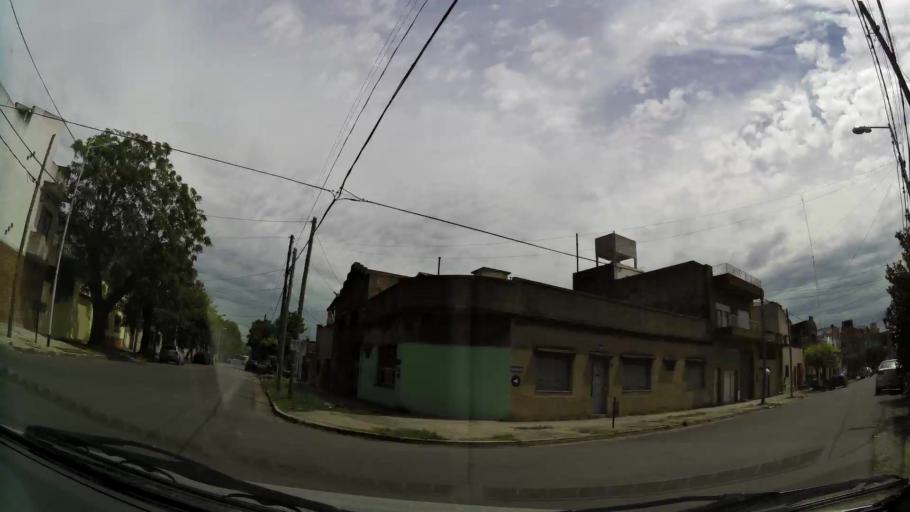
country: AR
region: Buenos Aires
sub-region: Partido de Avellaneda
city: Avellaneda
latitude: -34.6699
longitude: -58.3958
